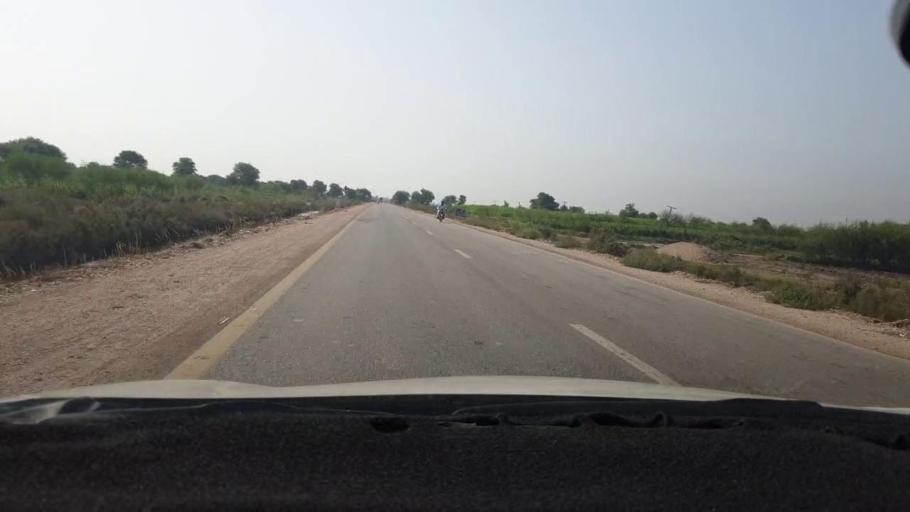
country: PK
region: Sindh
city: Sanghar
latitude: 26.0153
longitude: 68.9578
